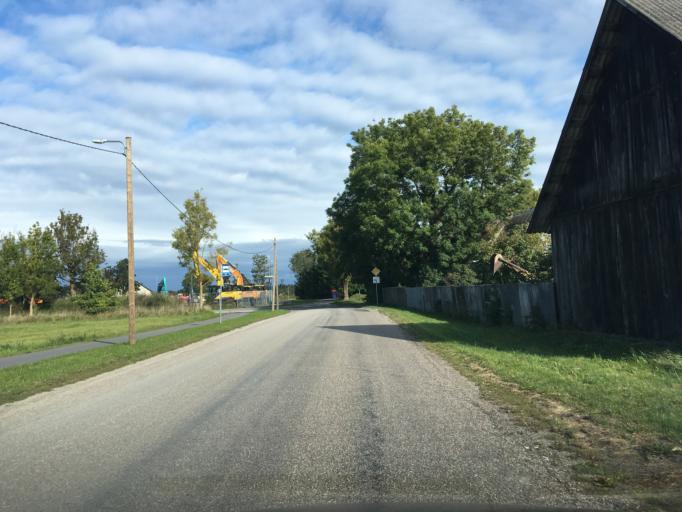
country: EE
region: Harju
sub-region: Saku vald
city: Saku
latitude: 59.3361
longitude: 24.6503
